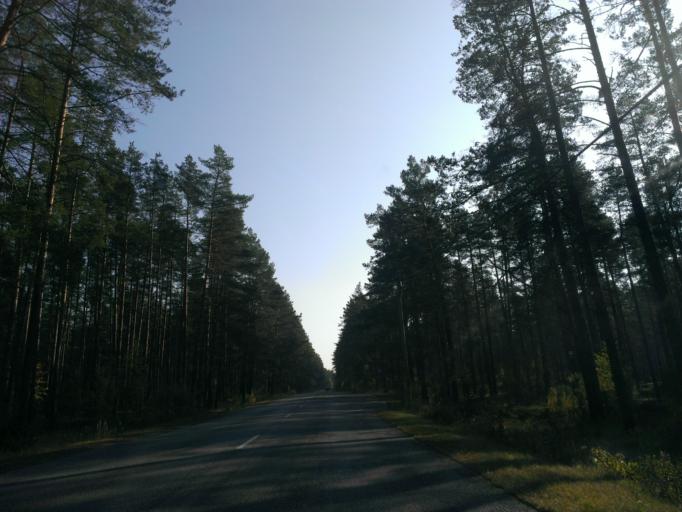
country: LV
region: Garkalne
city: Garkalne
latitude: 57.0301
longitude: 24.4258
